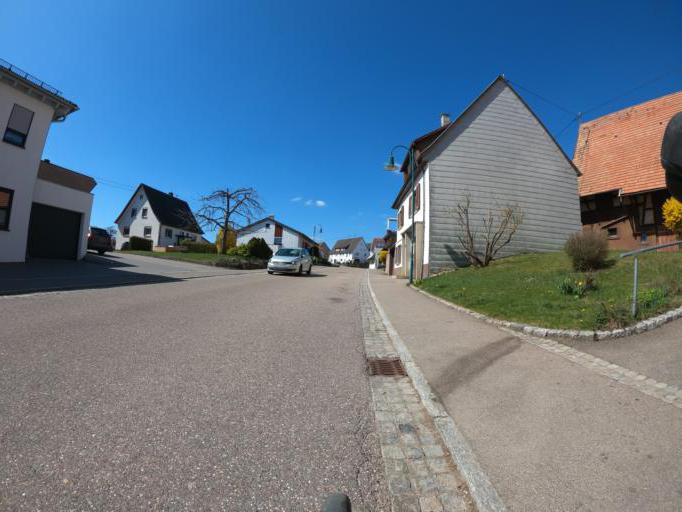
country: DE
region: Baden-Wuerttemberg
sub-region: Karlsruhe Region
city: Horb am Neckar
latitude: 48.4345
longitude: 8.7065
